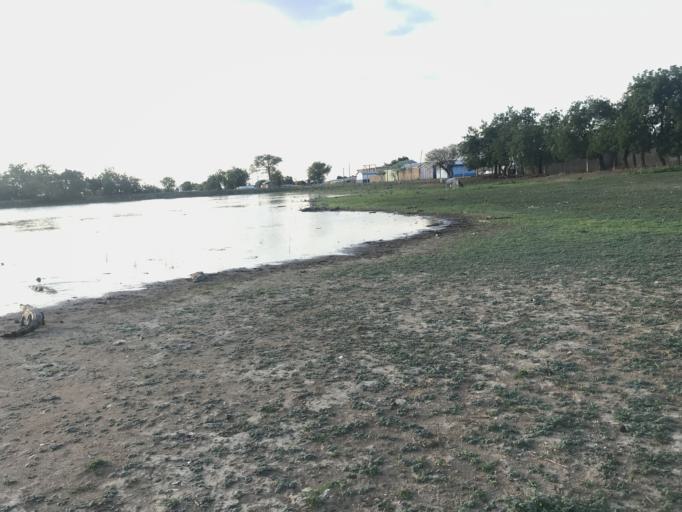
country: GH
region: Upper East
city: Navrongo
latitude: 10.9845
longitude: -1.1085
